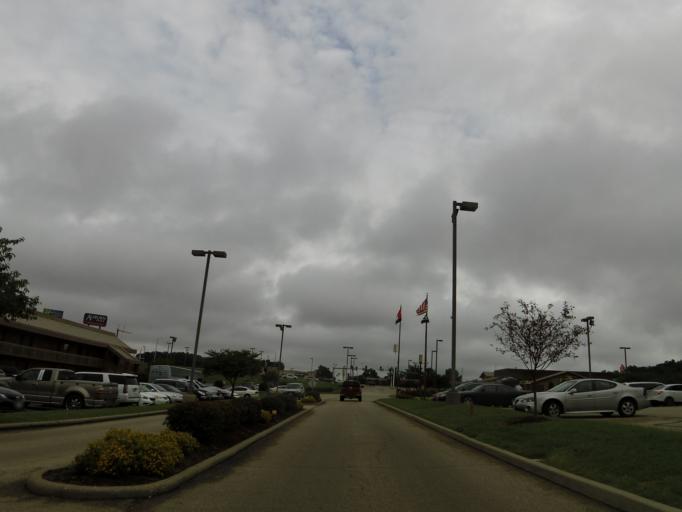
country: US
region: Missouri
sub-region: Cape Girardeau County
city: Cape Girardeau
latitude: 37.3009
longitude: -89.5773
